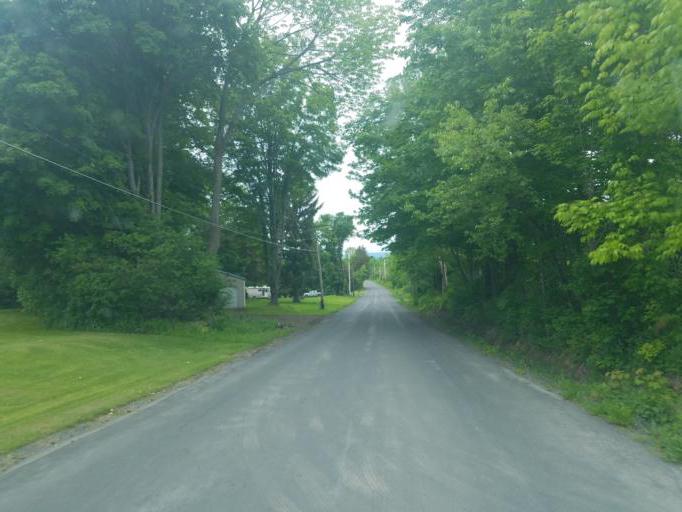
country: US
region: New York
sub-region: Herkimer County
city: Mohawk
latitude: 42.9766
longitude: -75.0171
